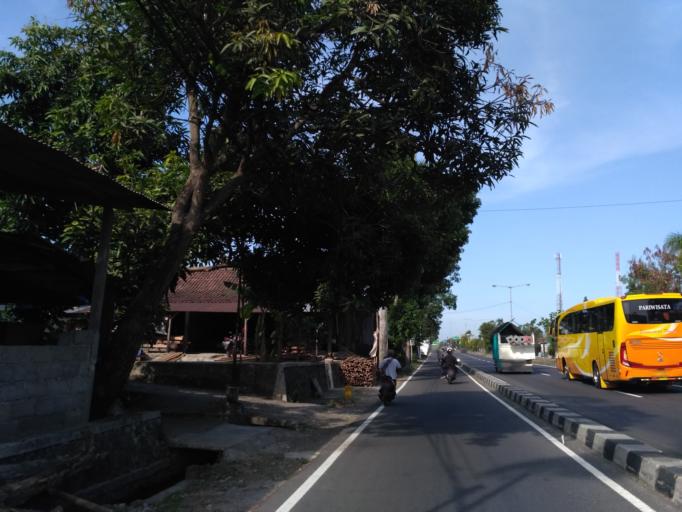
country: ID
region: Daerah Istimewa Yogyakarta
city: Kasihan
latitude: -7.8260
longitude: 110.3418
